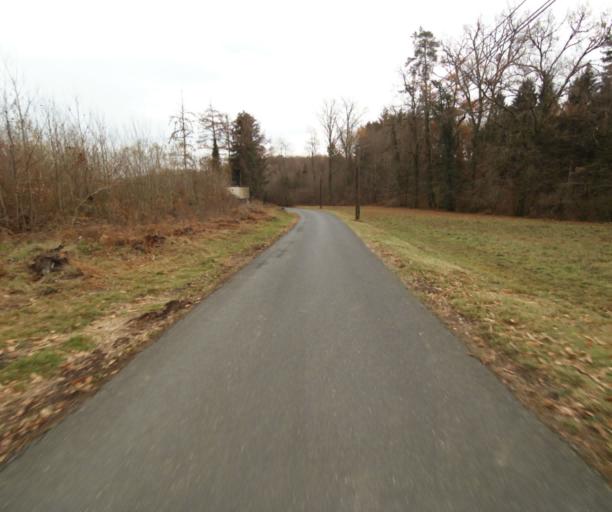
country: FR
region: Limousin
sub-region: Departement de la Correze
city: Chameyrat
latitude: 45.2375
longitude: 1.6751
